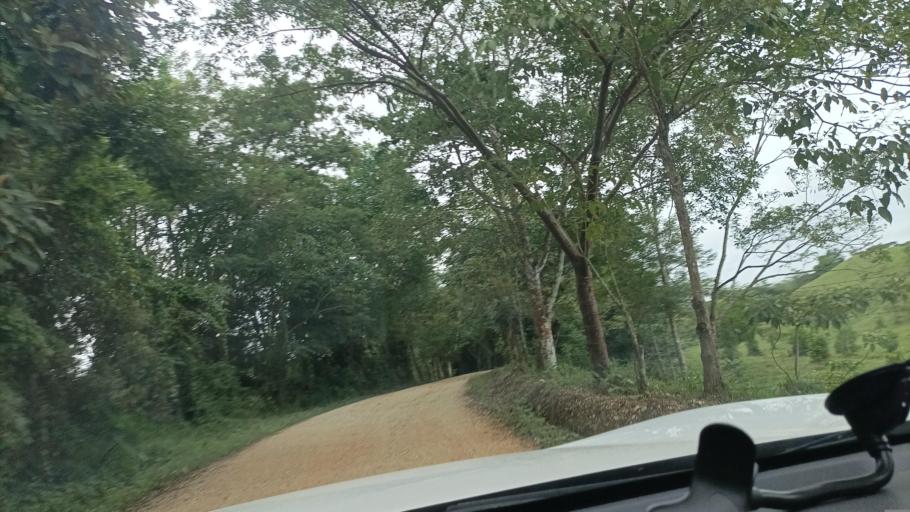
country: MX
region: Veracruz
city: Hidalgotitlan
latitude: 17.6082
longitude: -94.5244
